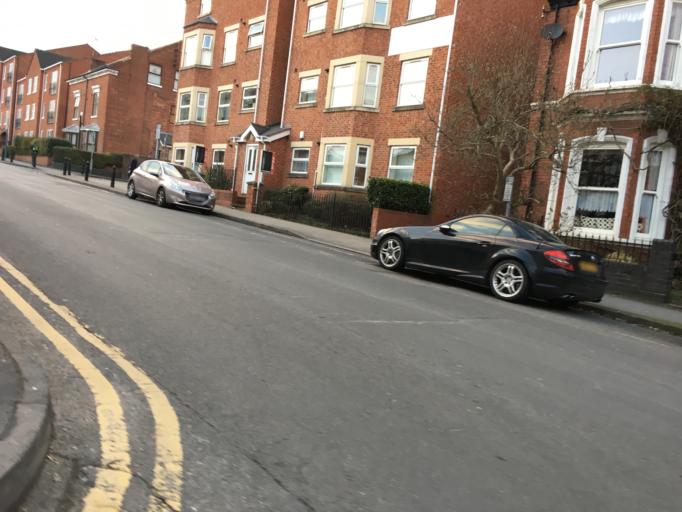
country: GB
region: England
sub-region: Warwickshire
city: Rugby
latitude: 52.3756
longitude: -1.2573
